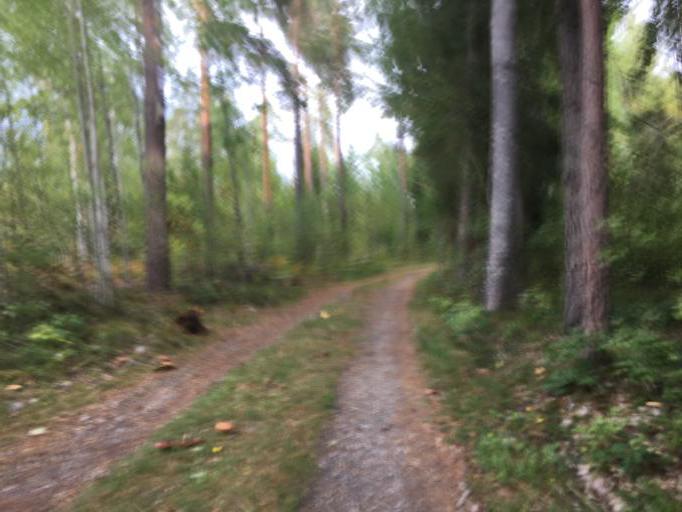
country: SE
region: Soedermanland
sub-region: Eskilstuna Kommun
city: Eskilstuna
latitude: 59.4575
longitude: 16.6515
